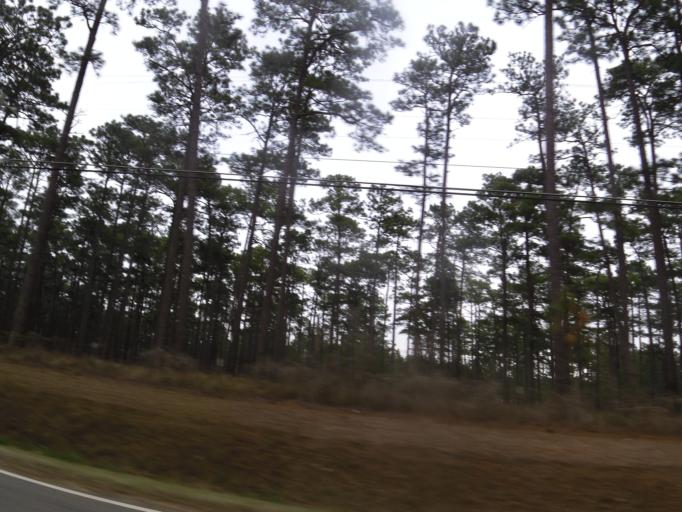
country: US
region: Georgia
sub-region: Thomas County
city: Thomasville
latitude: 30.8532
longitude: -84.0122
